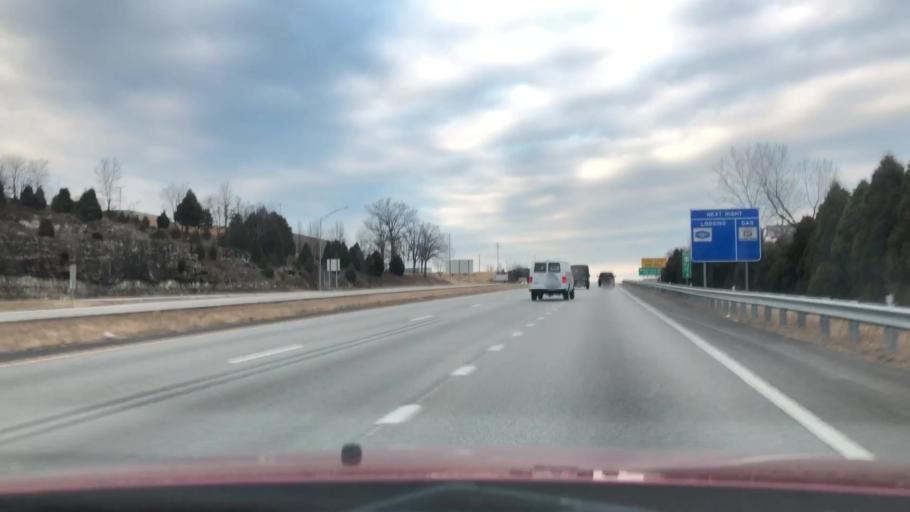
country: US
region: Missouri
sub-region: Taney County
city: Branson
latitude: 36.6596
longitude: -93.2219
